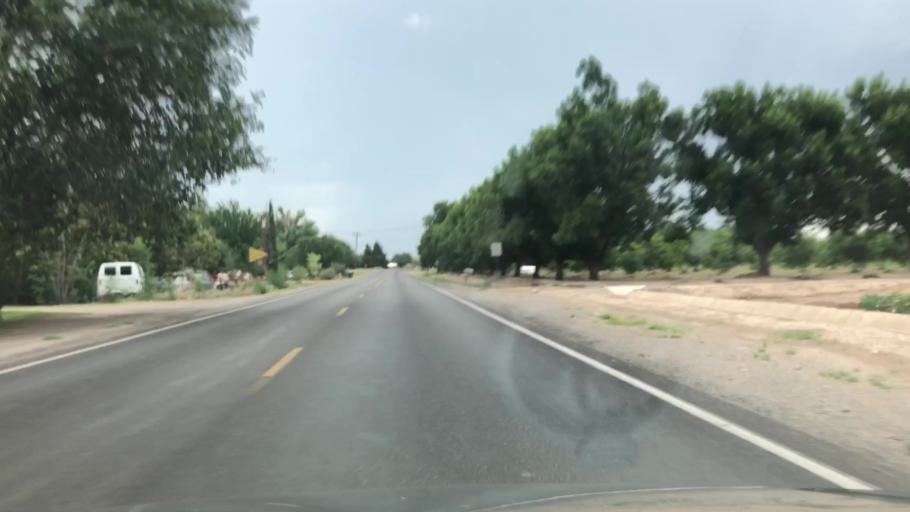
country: US
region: New Mexico
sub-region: Dona Ana County
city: La Union
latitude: 31.9801
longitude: -106.6514
